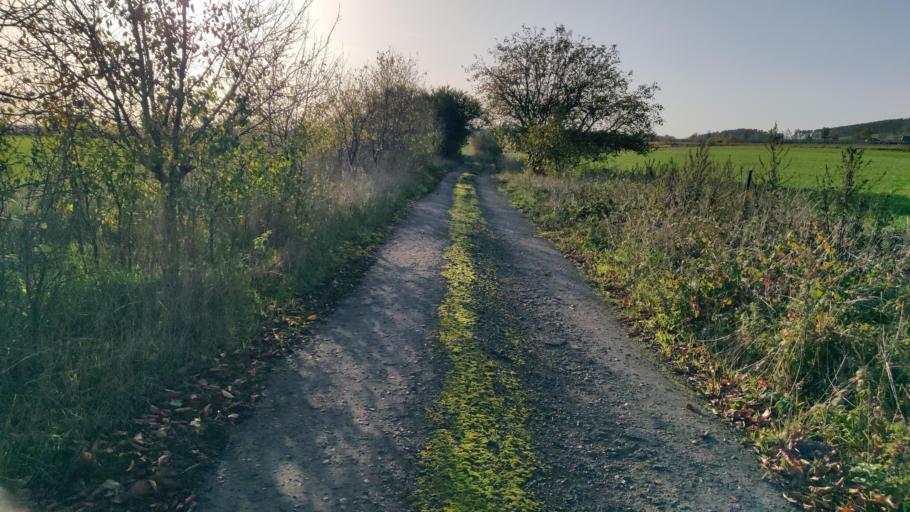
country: DE
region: Brandenburg
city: Grosskmehlen
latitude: 51.3596
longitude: 13.7359
